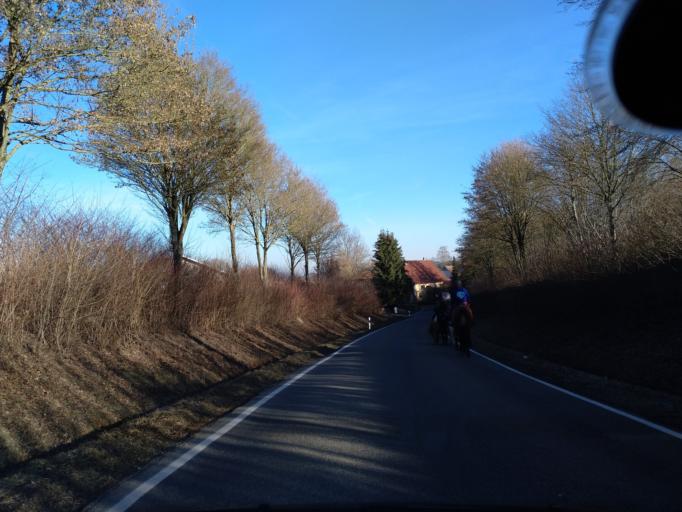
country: DE
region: Baden-Wuerttemberg
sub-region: Regierungsbezirk Stuttgart
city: Rosenberg
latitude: 49.0727
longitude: 9.9784
